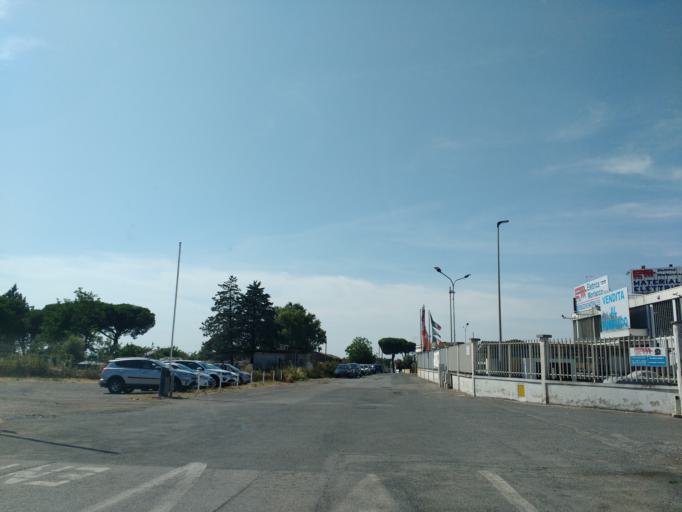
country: IT
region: Latium
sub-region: Citta metropolitana di Roma Capitale
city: Ciampino
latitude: 41.7798
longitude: 12.6053
